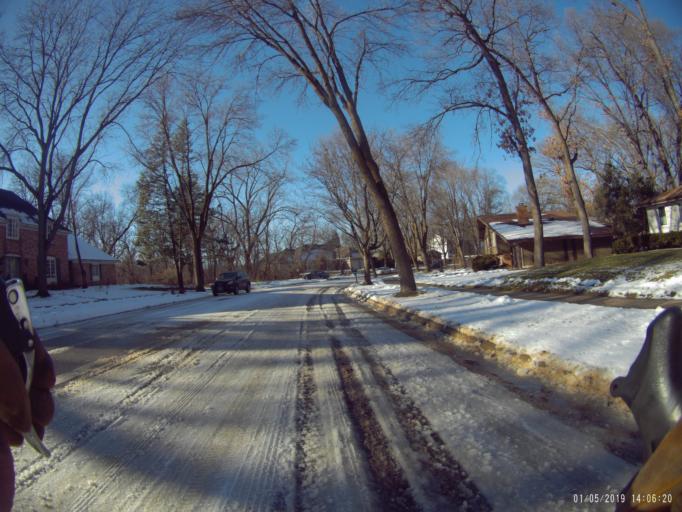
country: US
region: Wisconsin
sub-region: Dane County
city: Shorewood Hills
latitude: 43.0256
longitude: -89.4341
